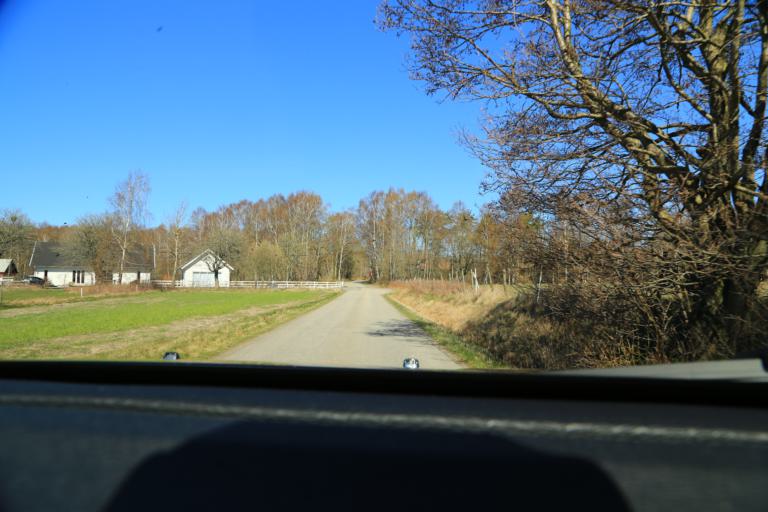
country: SE
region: Halland
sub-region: Varbergs Kommun
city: Traslovslage
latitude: 57.0917
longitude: 12.2853
